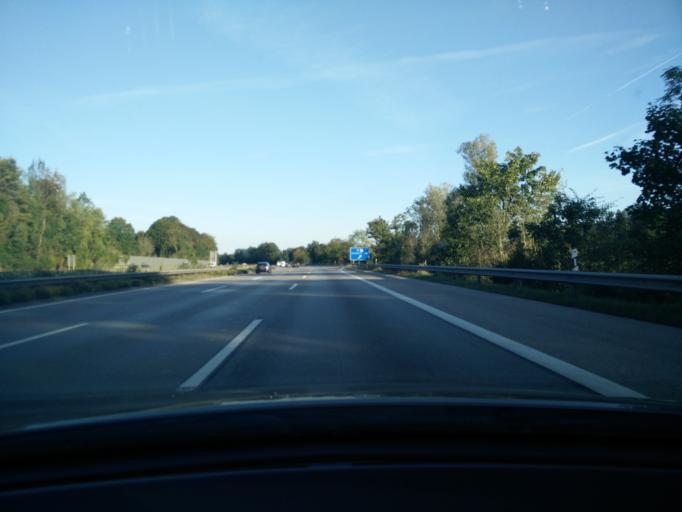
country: DE
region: Bavaria
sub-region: Upper Bavaria
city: Vagen
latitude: 47.8540
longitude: 11.8613
